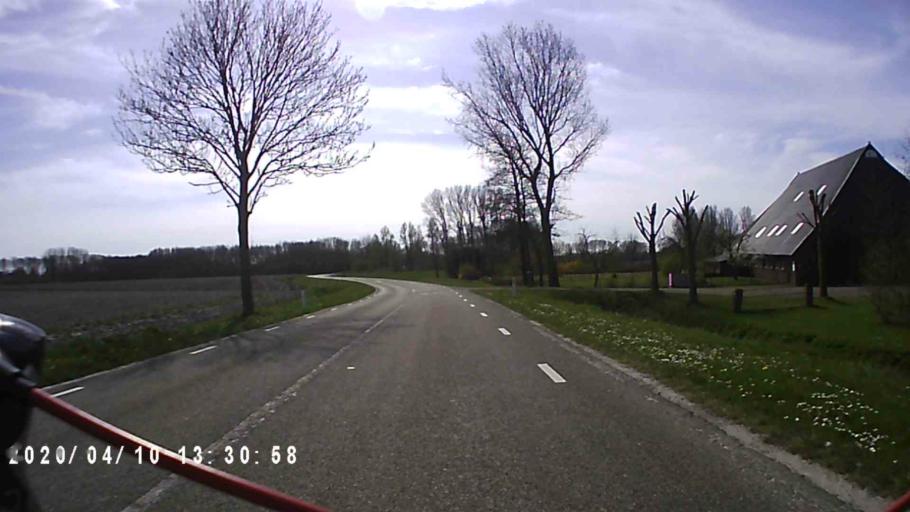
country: NL
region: Groningen
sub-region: Gemeente Zuidhorn
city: Oldehove
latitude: 53.3671
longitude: 6.4190
